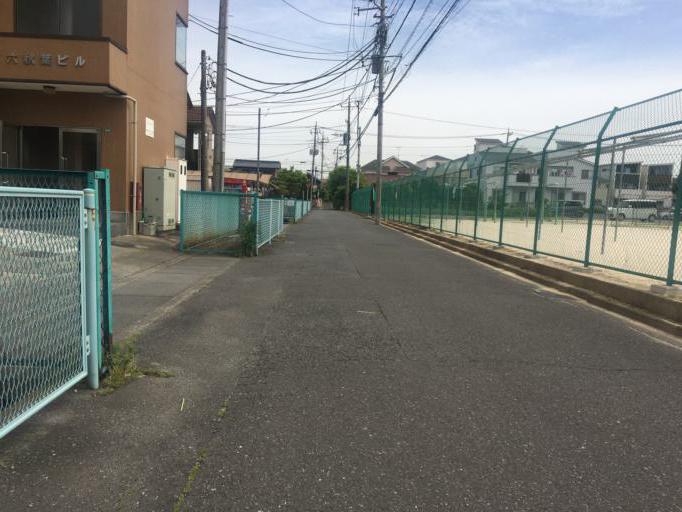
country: JP
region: Saitama
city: Yono
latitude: 35.8619
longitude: 139.6126
